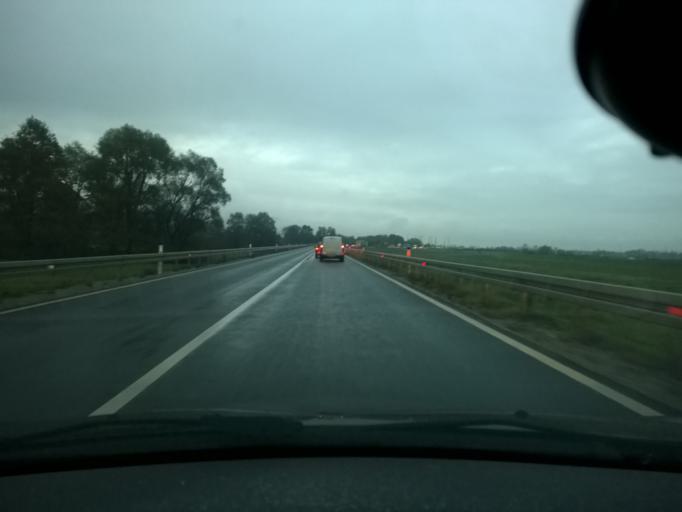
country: HR
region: Zagrebacka
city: Pojatno
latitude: 45.8833
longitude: 15.8192
